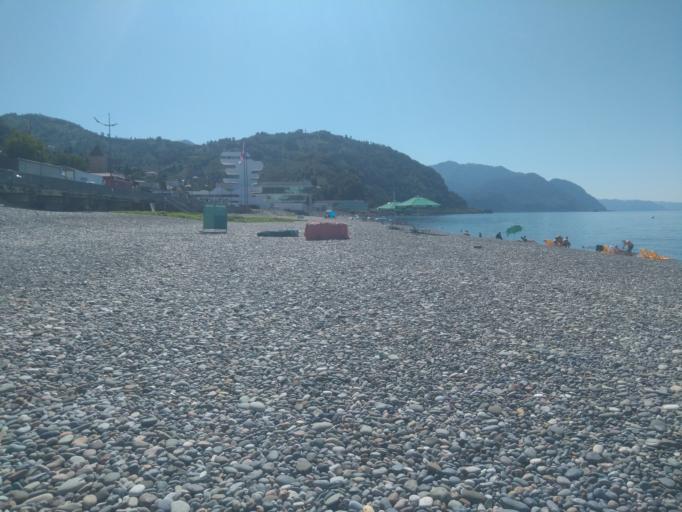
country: TR
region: Artvin
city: Kemalpasa
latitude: 41.5244
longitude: 41.5485
